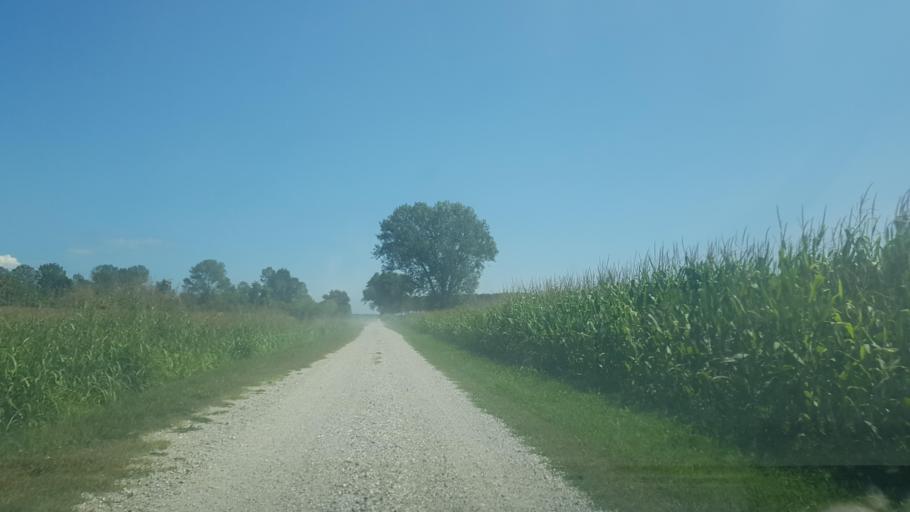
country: IT
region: Friuli Venezia Giulia
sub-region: Provincia di Udine
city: Pocenia
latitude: 45.8475
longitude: 13.1276
